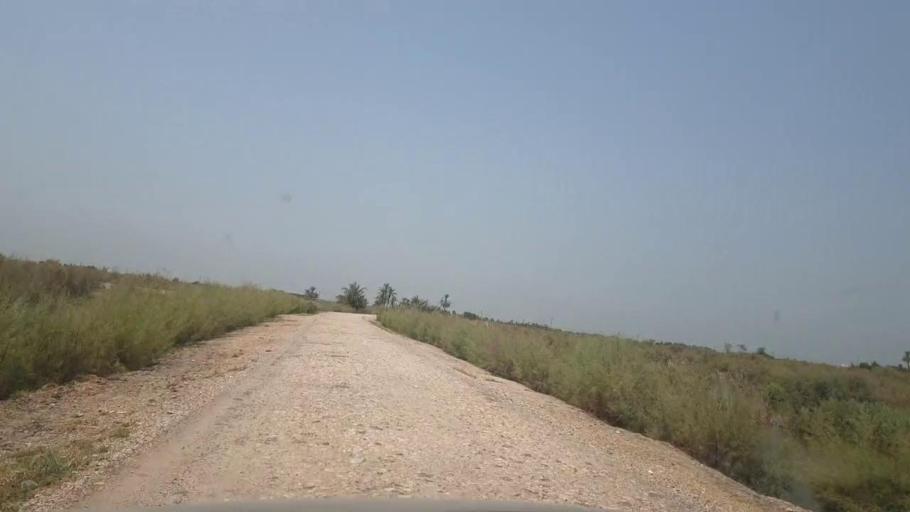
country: PK
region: Sindh
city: Lakhi
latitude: 27.8443
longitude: 68.6267
